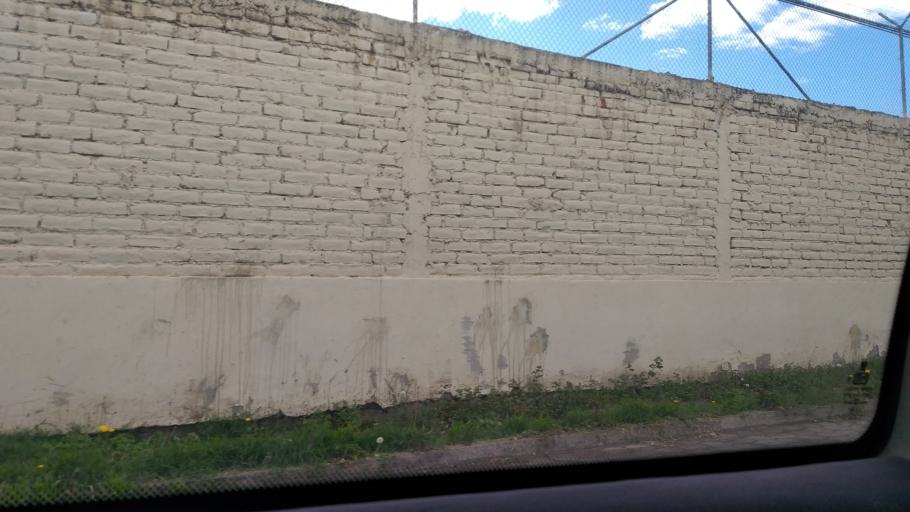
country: EC
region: Chimborazo
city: Riobamba
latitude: -1.6922
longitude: -78.6312
